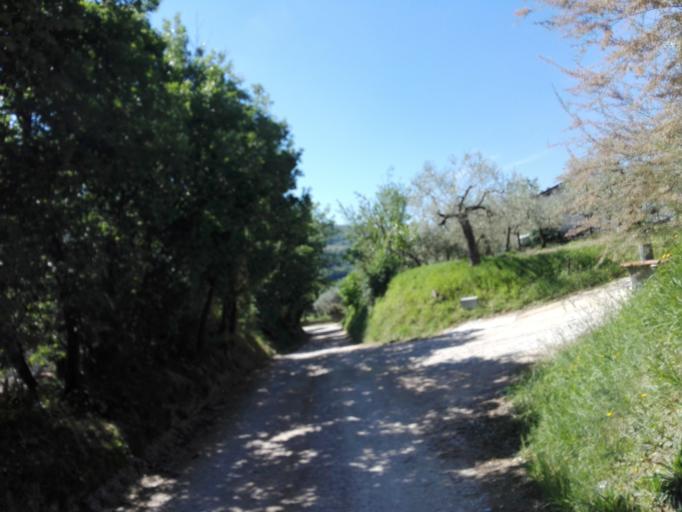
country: IT
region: Umbria
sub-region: Provincia di Perugia
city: Foligno
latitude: 42.9690
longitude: 12.7423
